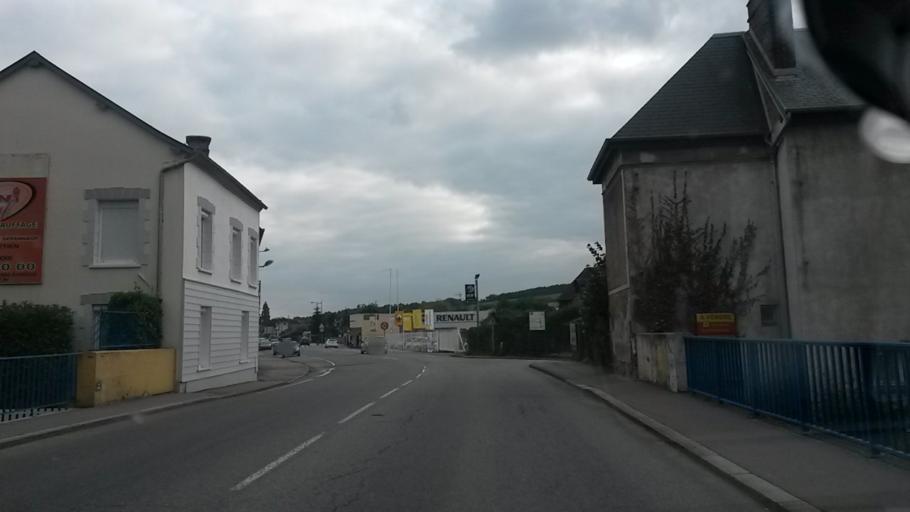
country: FR
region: Haute-Normandie
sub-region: Departement de l'Eure
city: Gravigny
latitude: 49.0464
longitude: 1.1619
